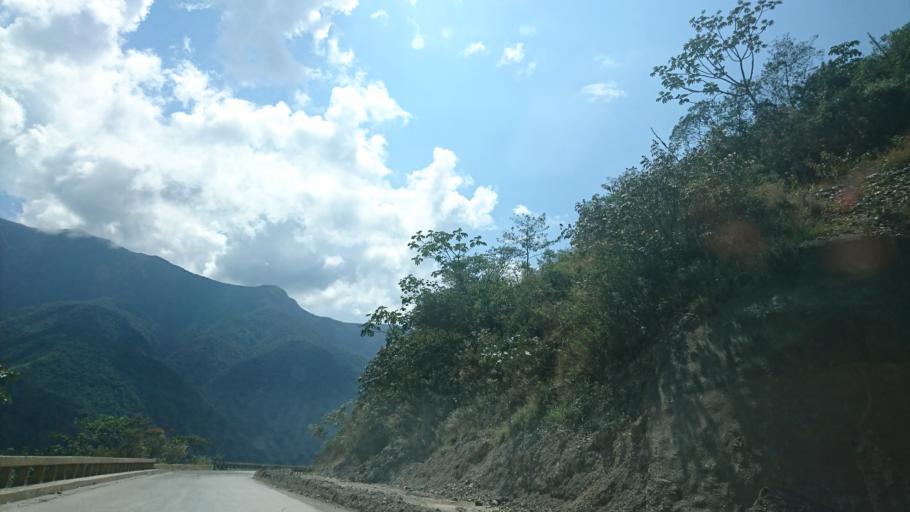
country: BO
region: La Paz
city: Coroico
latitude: -16.2098
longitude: -67.7888
